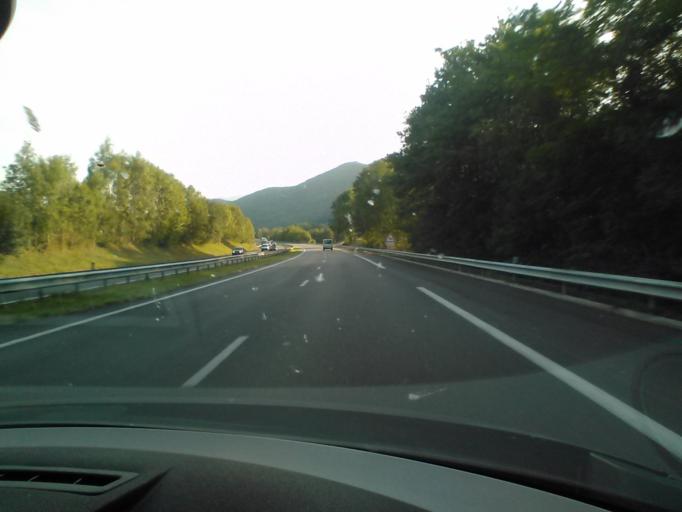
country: FR
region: Rhone-Alpes
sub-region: Departement de la Savoie
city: La Biolle
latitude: 45.7468
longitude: 5.9314
